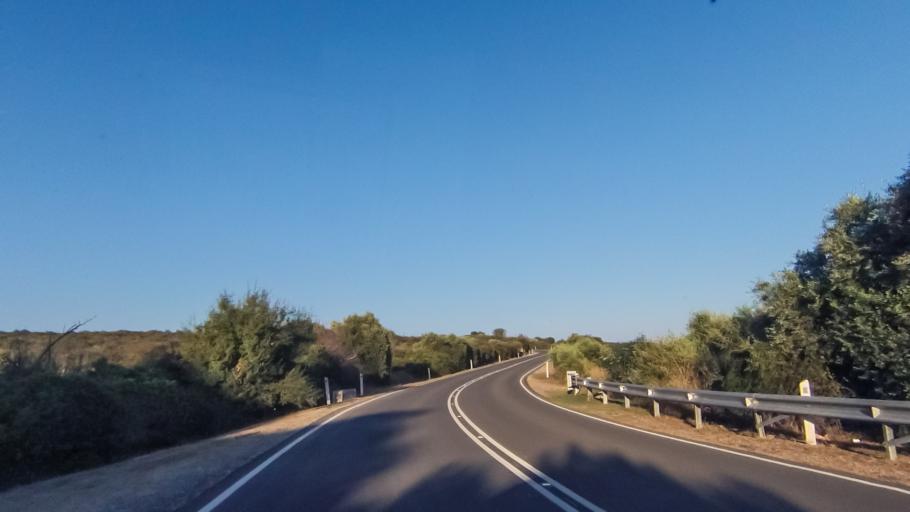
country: CY
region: Limassol
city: Sotira
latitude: 34.6754
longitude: 32.8064
